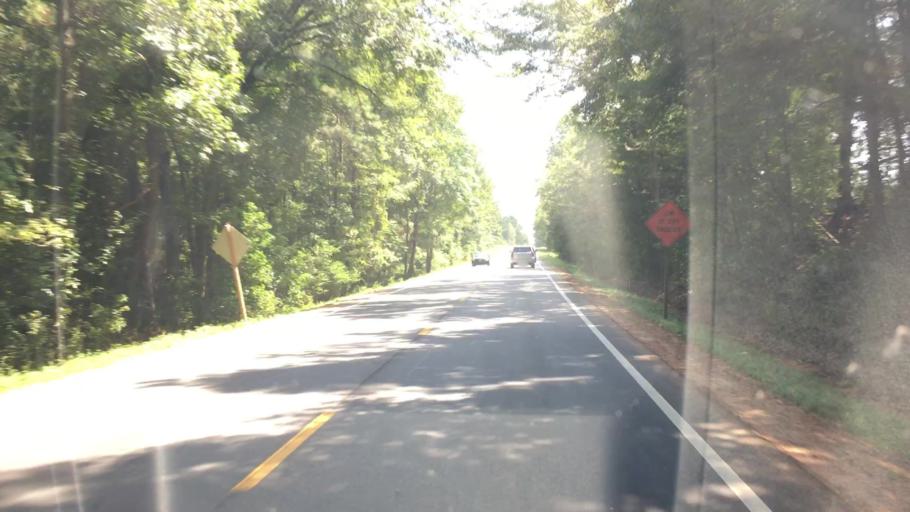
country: US
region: Georgia
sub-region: Oconee County
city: Watkinsville
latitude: 33.7884
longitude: -83.4239
